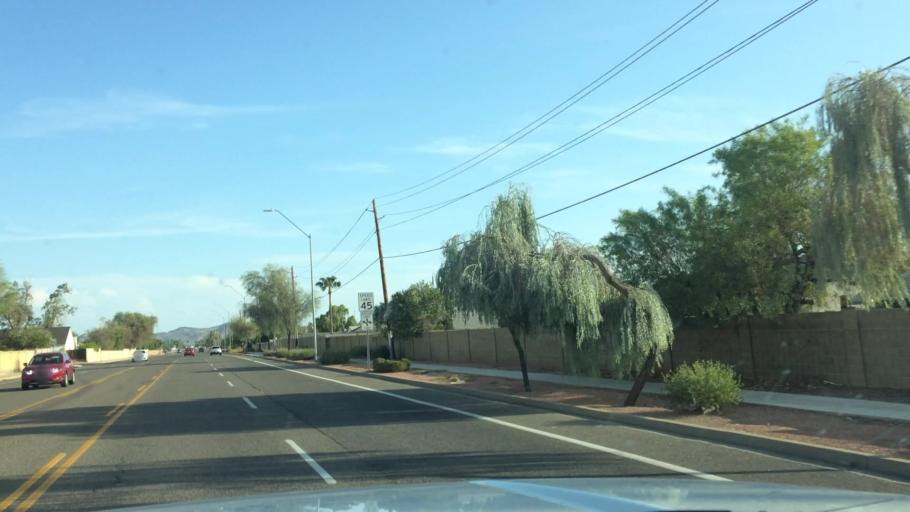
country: US
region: Arizona
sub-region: Maricopa County
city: Glendale
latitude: 33.6758
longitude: -112.0829
